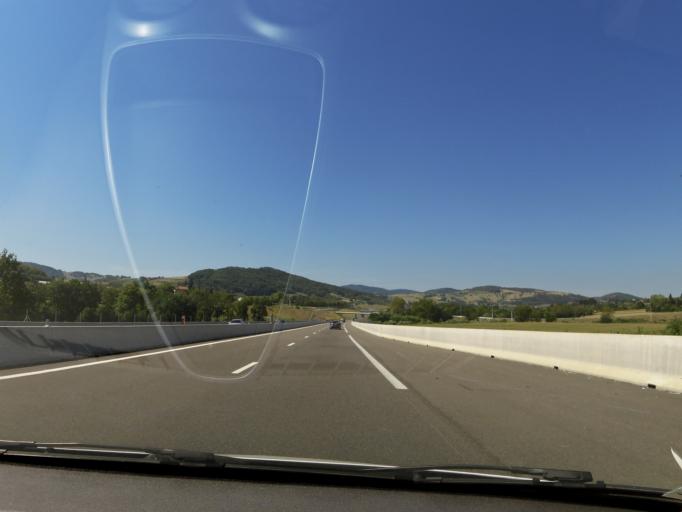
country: FR
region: Rhone-Alpes
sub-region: Departement du Rhone
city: Saint-Romain-de-Popey
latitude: 45.8753
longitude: 4.5251
